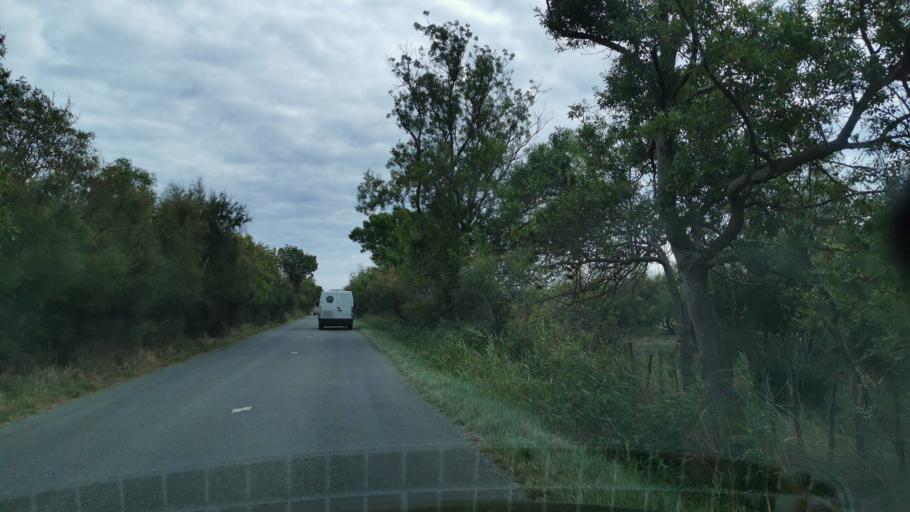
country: FR
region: Languedoc-Roussillon
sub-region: Departement de l'Herault
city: Vendres
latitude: 43.2324
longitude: 3.1957
